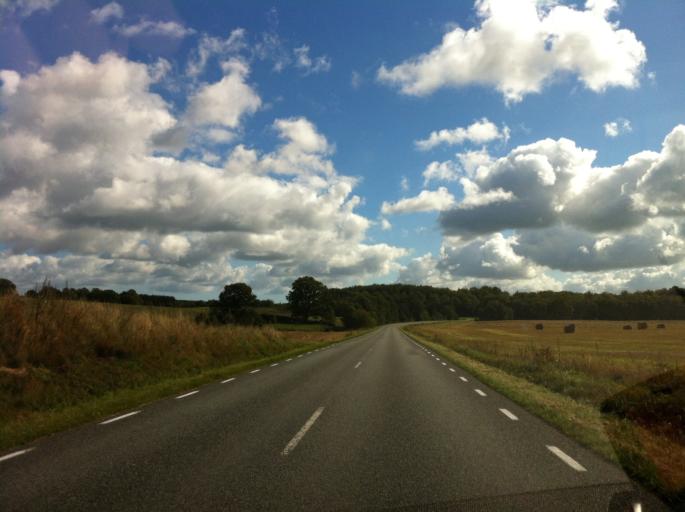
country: SE
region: Skane
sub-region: Kristianstads Kommun
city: Degeberga
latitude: 55.7856
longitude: 13.8712
